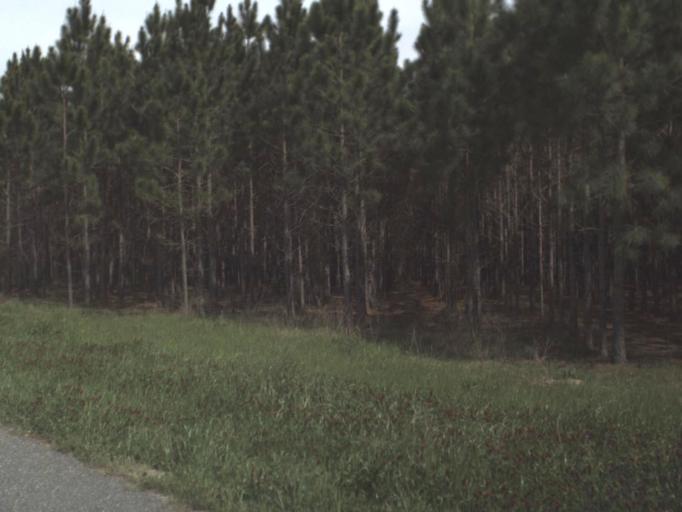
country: US
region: Florida
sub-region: Jackson County
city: Malone
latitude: 30.9600
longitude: -85.1269
